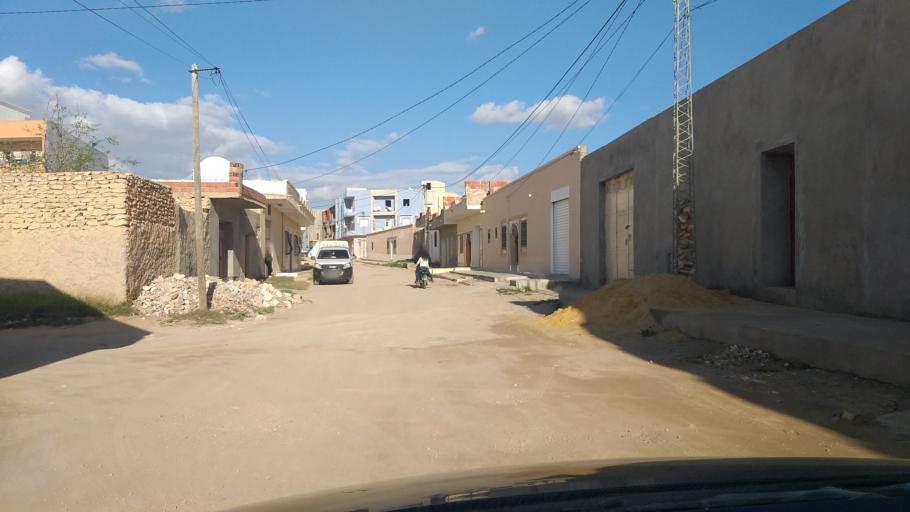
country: TN
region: Al Mahdiyah
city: El Jem
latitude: 35.2899
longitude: 10.7127
